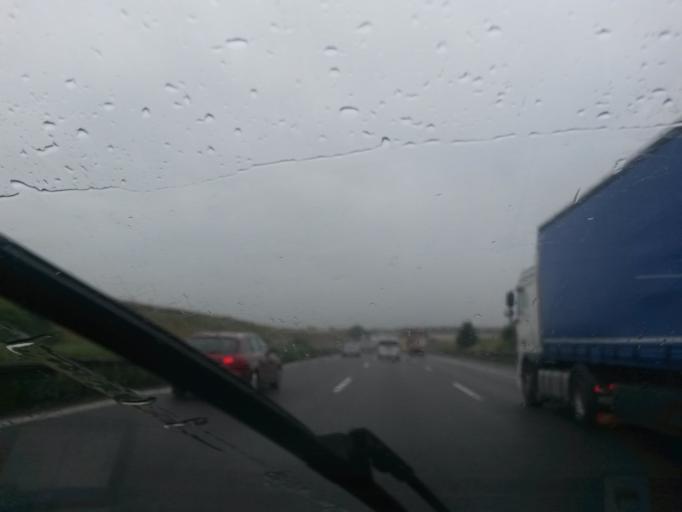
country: DE
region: Bavaria
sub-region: Upper Bavaria
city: Stammham
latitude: 48.8609
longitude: 11.4660
